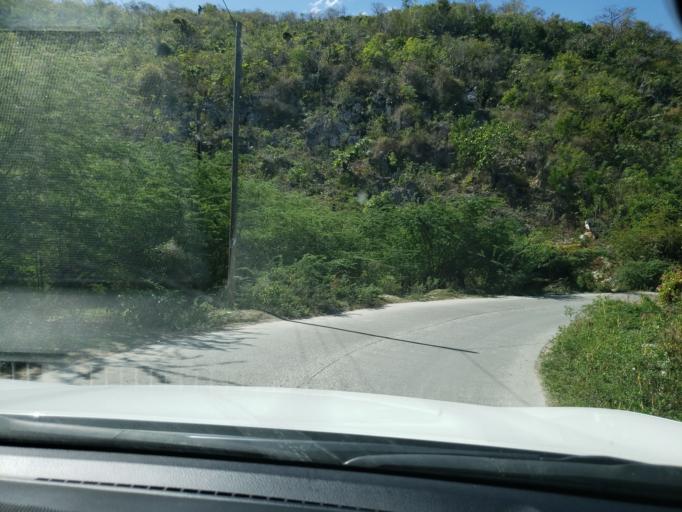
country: HT
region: Nippes
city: Miragoane
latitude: 18.4441
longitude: -73.1005
